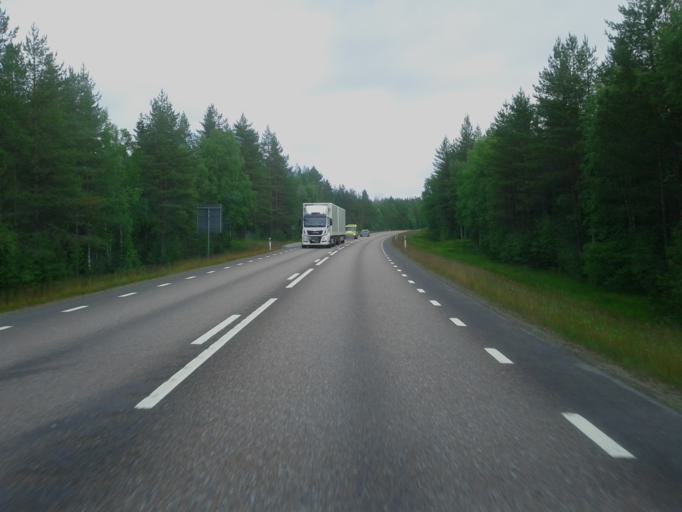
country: SE
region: Vaesterbotten
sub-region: Skelleftea Kommun
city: Burea
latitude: 64.3317
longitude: 21.2043
